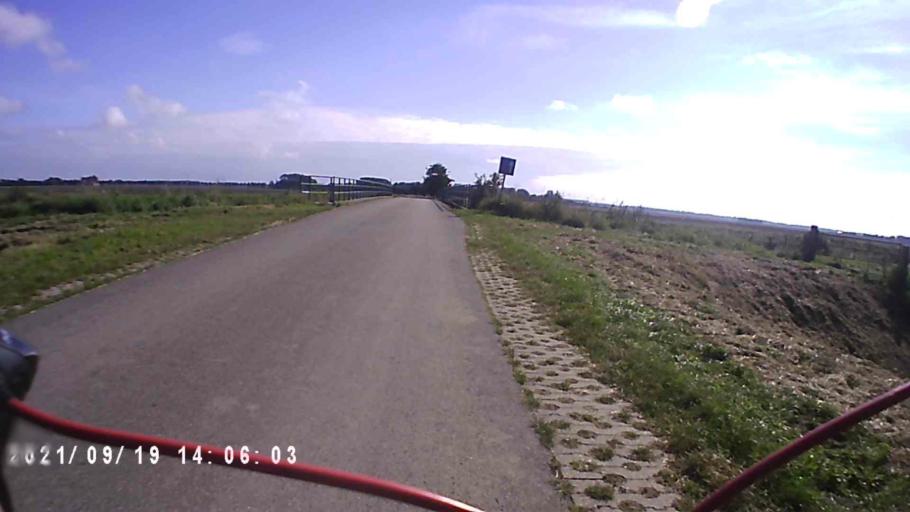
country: NL
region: Groningen
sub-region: Gemeente  Oldambt
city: Winschoten
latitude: 53.1433
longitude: 7.1252
